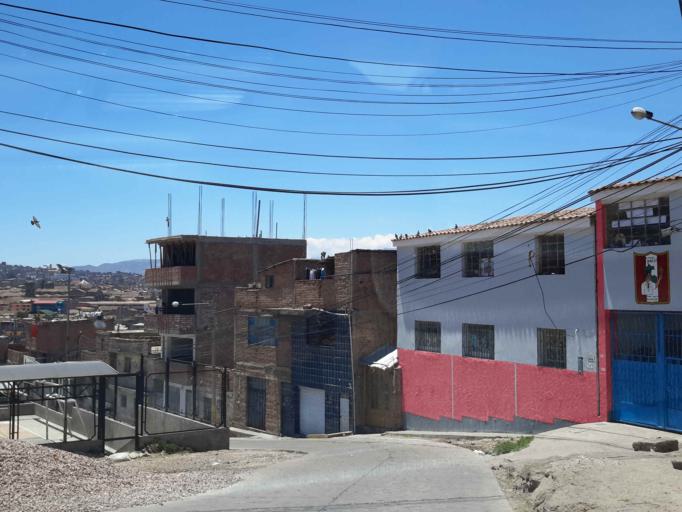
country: PE
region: Ayacucho
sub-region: Provincia de Huamanga
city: Ayacucho
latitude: -13.1675
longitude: -74.2231
